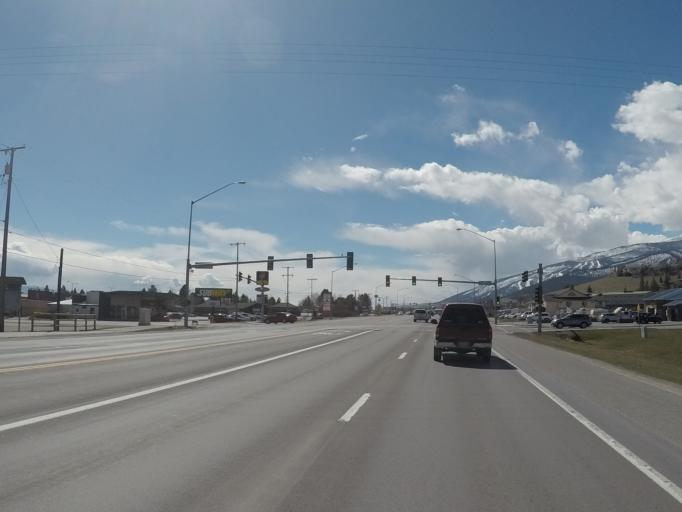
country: US
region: Montana
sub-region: Missoula County
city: Lolo
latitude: 46.7658
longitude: -114.0803
